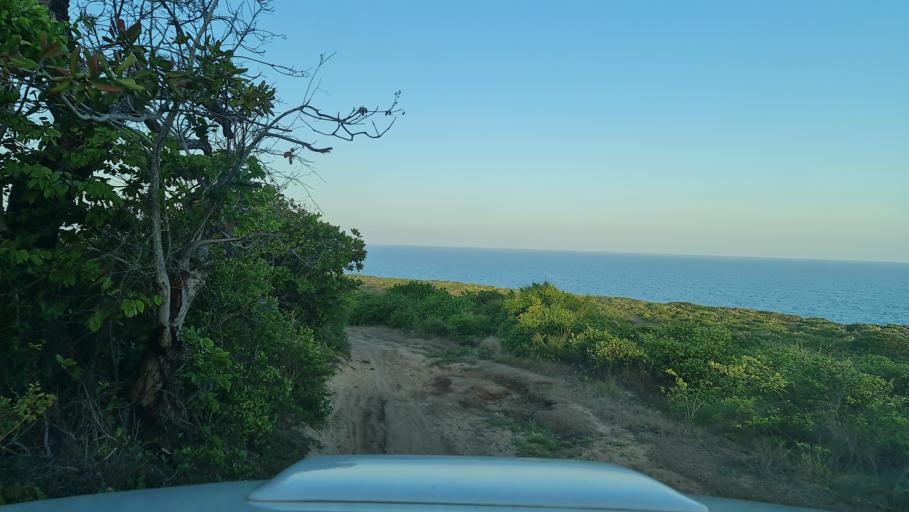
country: MZ
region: Nampula
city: Ilha de Mocambique
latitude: -15.6349
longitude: 40.4159
